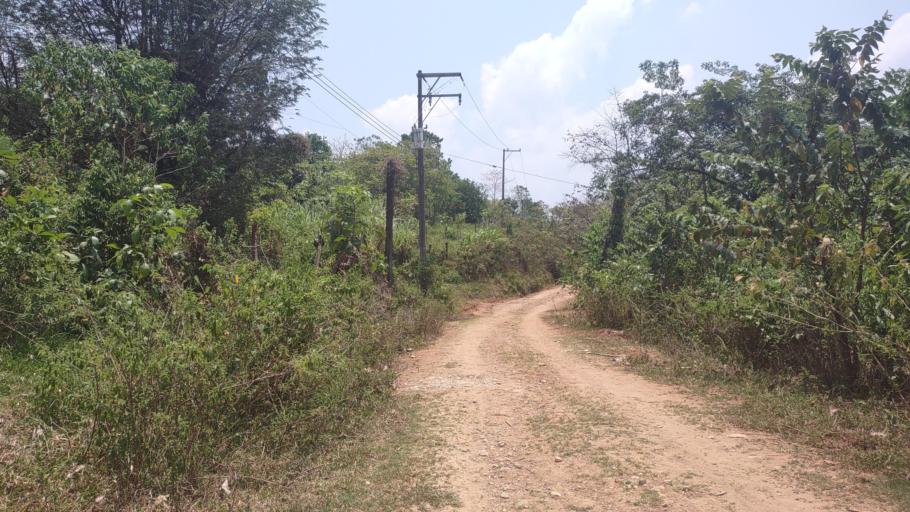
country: MX
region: Tabasco
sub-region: Huimanguillo
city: Francisco Rueda
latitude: 17.6499
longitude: -93.9066
